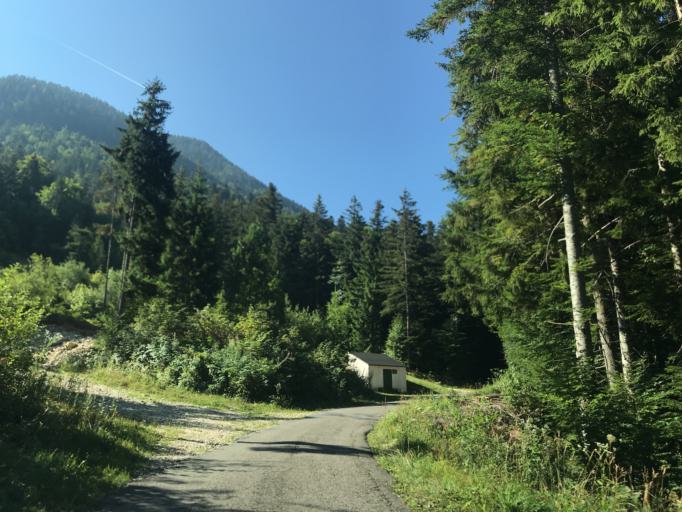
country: FR
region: Rhone-Alpes
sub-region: Departement de la Haute-Savoie
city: Thorens-Glieres
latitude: 45.9725
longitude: 6.2340
